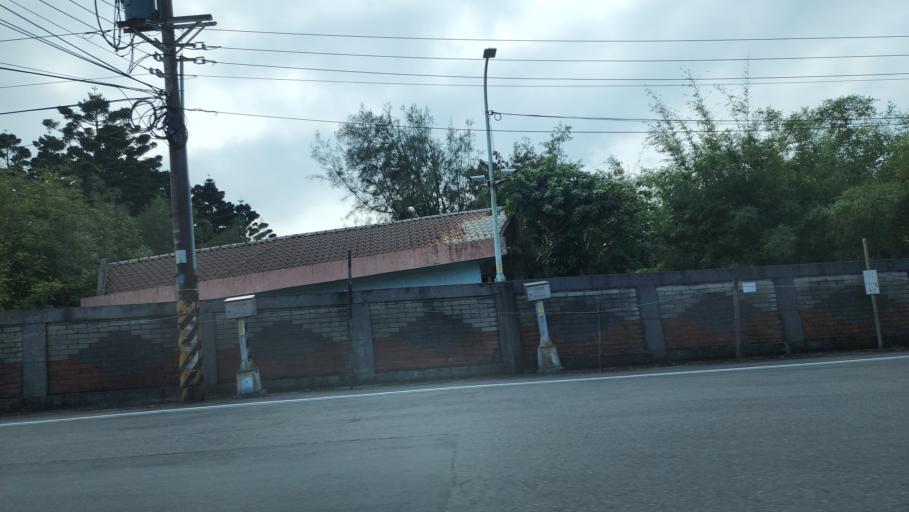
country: TW
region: Taiwan
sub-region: Keelung
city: Keelung
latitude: 25.2268
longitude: 121.6437
